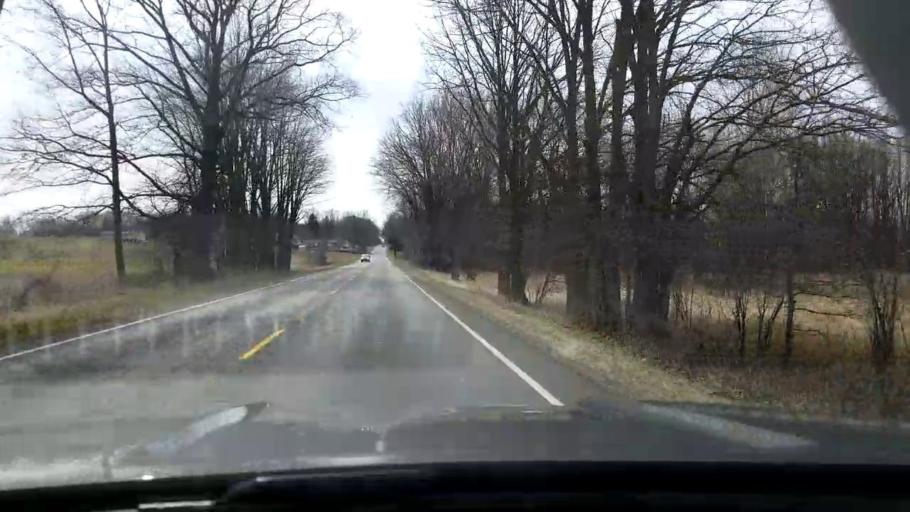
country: US
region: Michigan
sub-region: Jackson County
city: Spring Arbor
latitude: 42.1940
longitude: -84.5207
